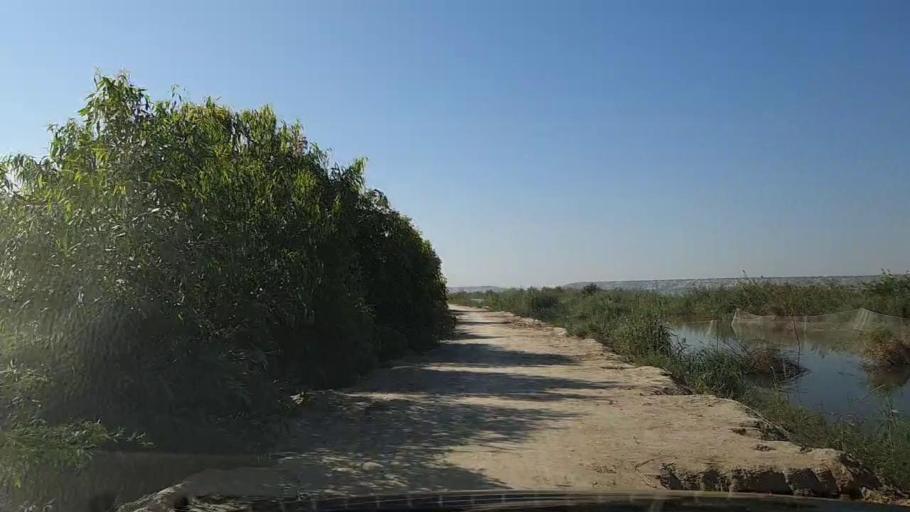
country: PK
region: Sindh
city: Thatta
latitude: 24.6971
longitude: 67.8968
